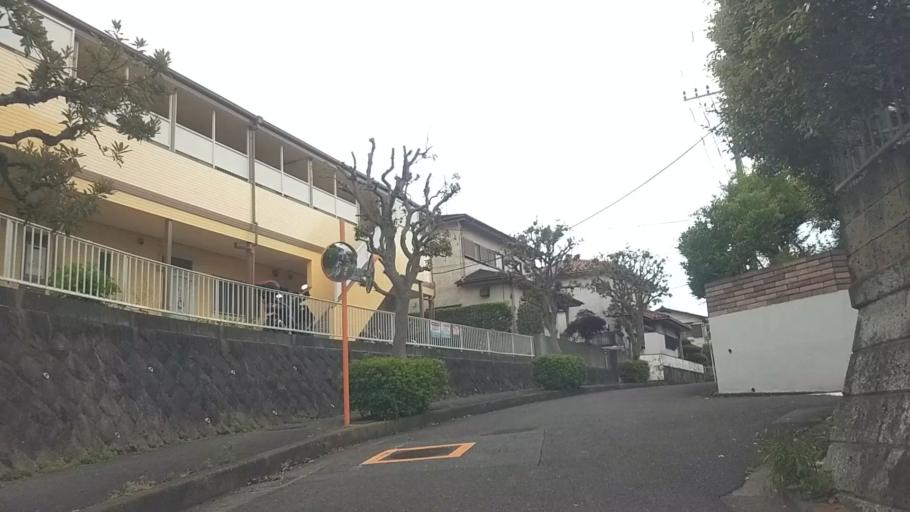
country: JP
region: Kanagawa
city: Fujisawa
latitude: 35.3572
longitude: 139.5068
